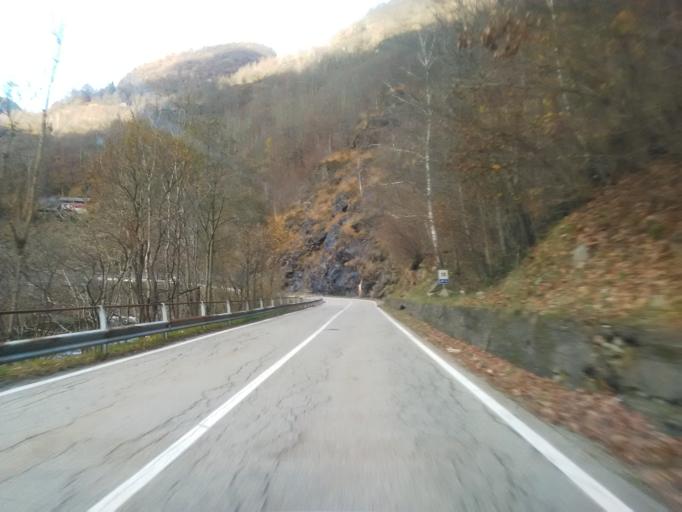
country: IT
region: Piedmont
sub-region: Provincia di Vercelli
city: Cravagliana
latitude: 45.8476
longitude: 8.1965
